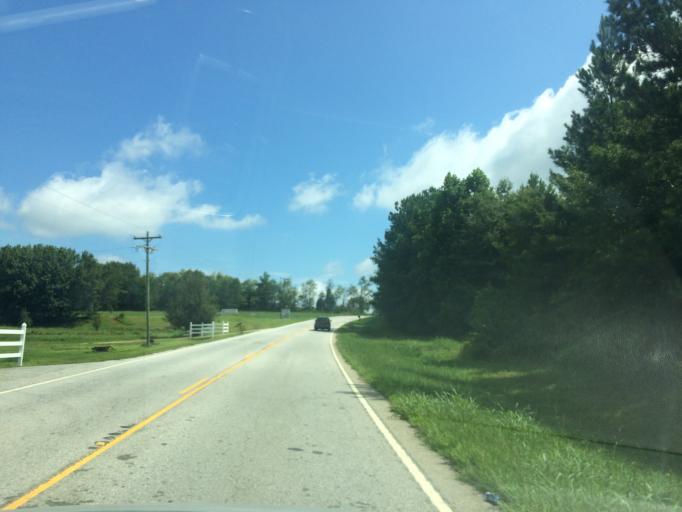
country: US
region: South Carolina
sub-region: Spartanburg County
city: Inman
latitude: 35.0729
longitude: -82.0741
